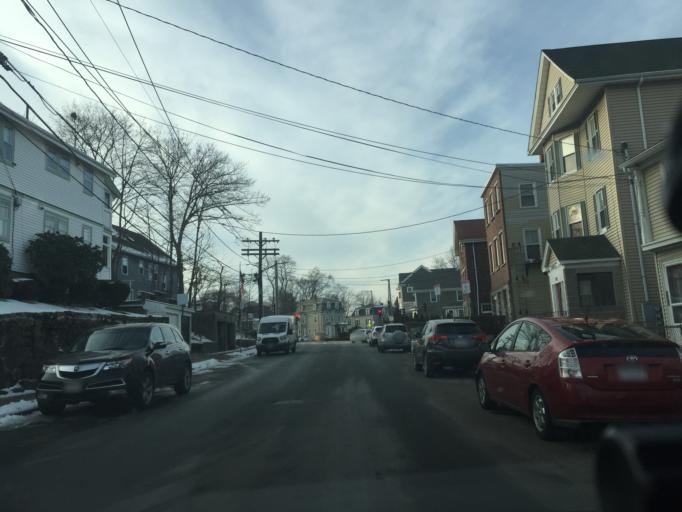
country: US
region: Massachusetts
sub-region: Norfolk County
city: Brookline
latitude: 42.3459
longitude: -71.1516
